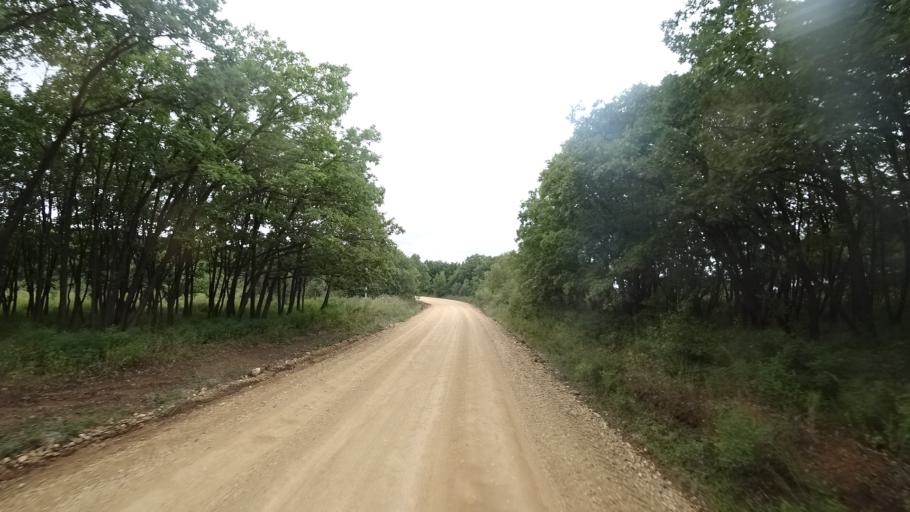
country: RU
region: Primorskiy
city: Chernigovka
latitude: 44.3407
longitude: 132.6209
